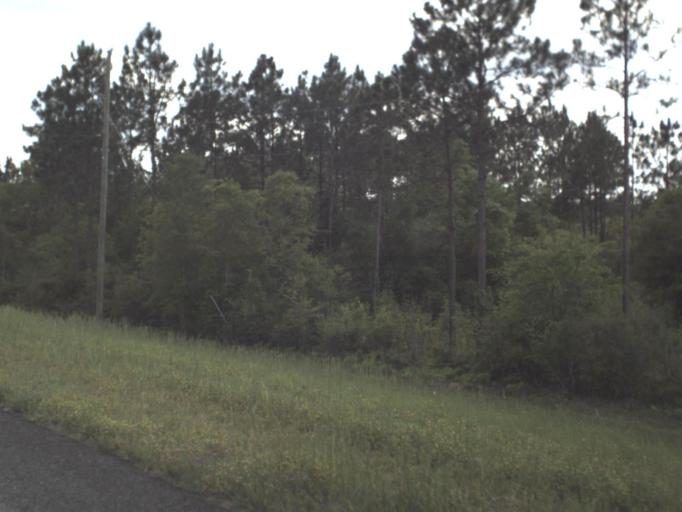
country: US
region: Florida
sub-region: Escambia County
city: Molino
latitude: 30.7650
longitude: -87.3412
